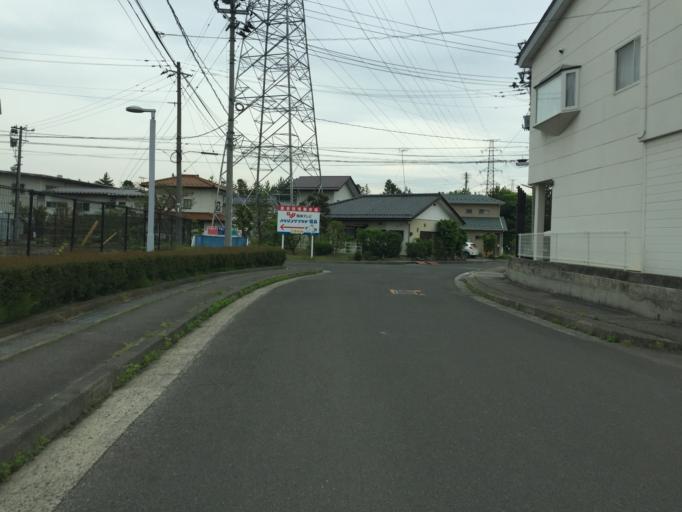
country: JP
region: Fukushima
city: Fukushima-shi
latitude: 37.8033
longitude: 140.4484
